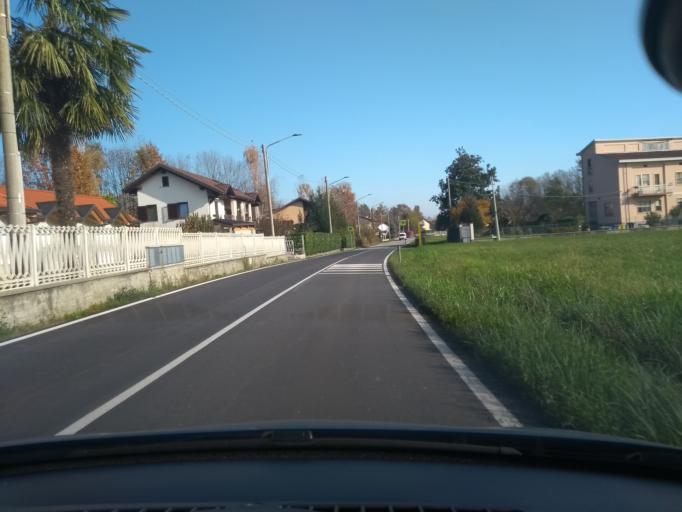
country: IT
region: Piedmont
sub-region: Provincia di Torino
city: Fiano
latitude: 45.2167
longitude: 7.5322
